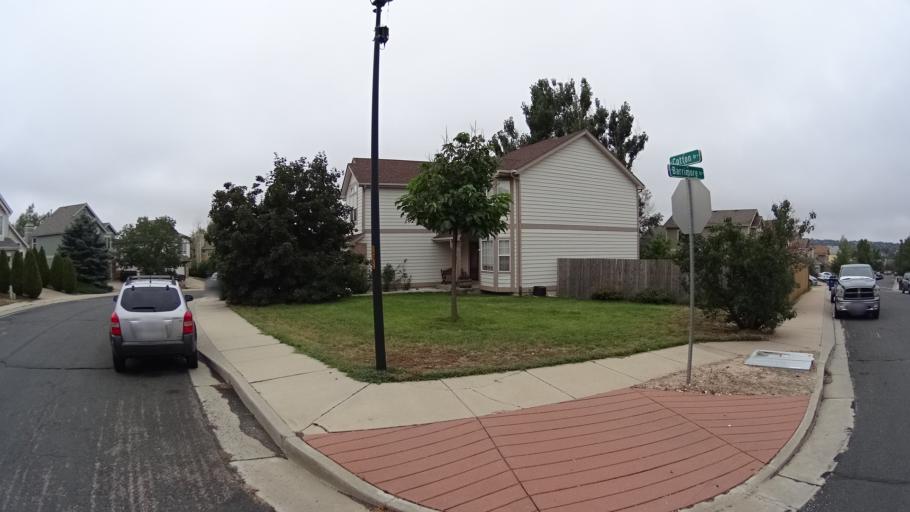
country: US
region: Colorado
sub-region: El Paso County
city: Cimarron Hills
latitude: 38.9349
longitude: -104.7512
